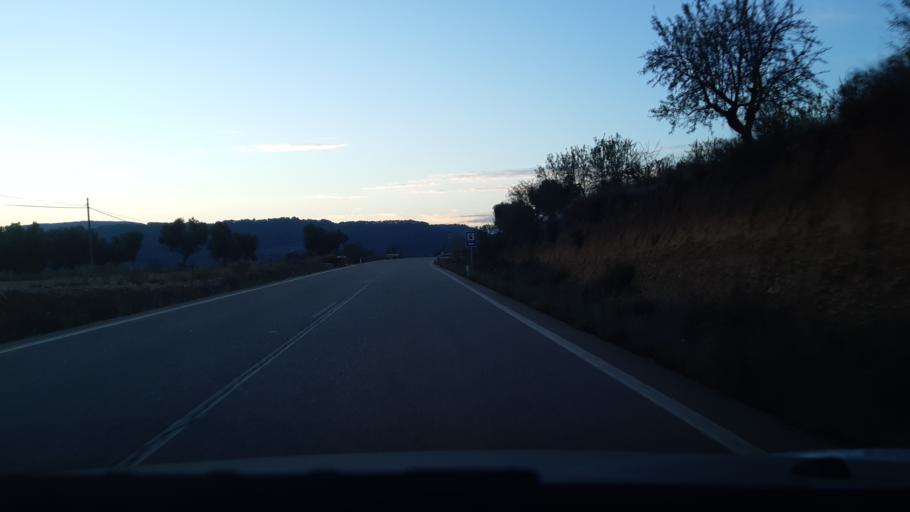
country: ES
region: Aragon
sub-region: Provincia de Teruel
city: Valderrobres
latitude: 40.8639
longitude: 0.1672
